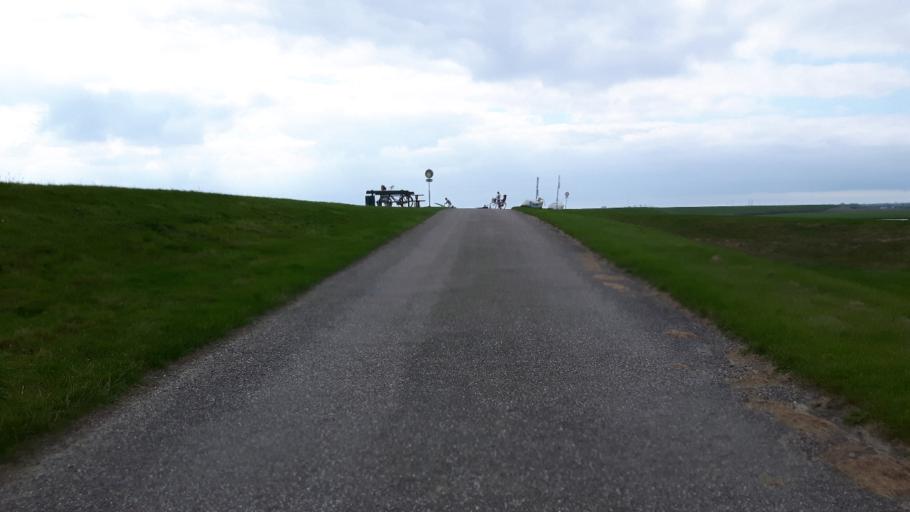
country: NL
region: Friesland
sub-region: Gemeente Ameland
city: Nes
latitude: 53.4385
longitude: 5.8073
